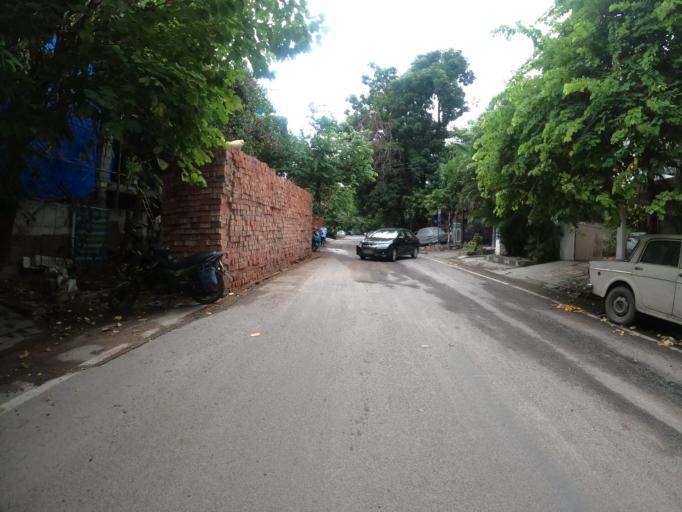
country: IN
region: Telangana
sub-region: Hyderabad
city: Hyderabad
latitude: 17.4222
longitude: 78.4069
